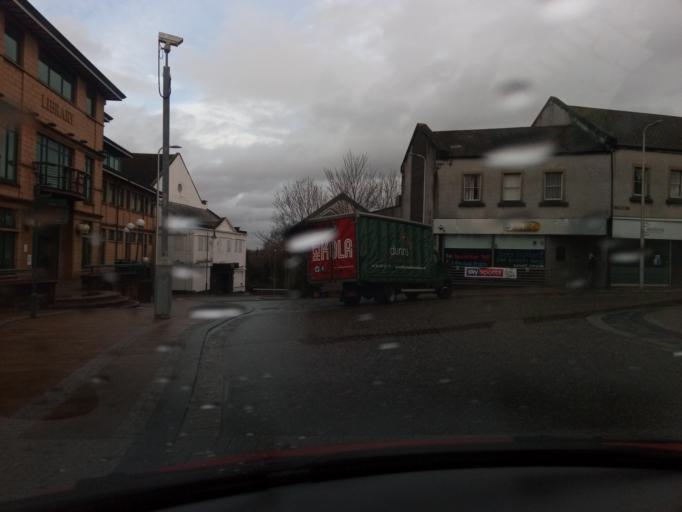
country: GB
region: Scotland
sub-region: East Dunbartonshire
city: Kirkintilloch
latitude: 55.9411
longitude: -4.1594
